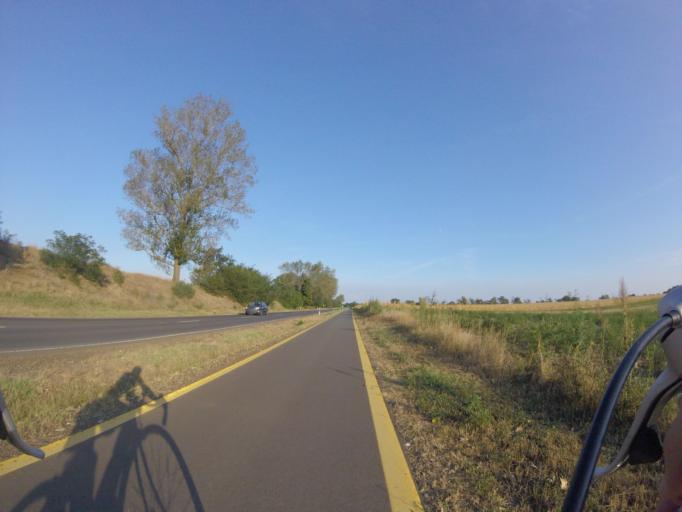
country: HU
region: Szabolcs-Szatmar-Bereg
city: Tiszanagyfalu
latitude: 48.0609
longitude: 21.5494
